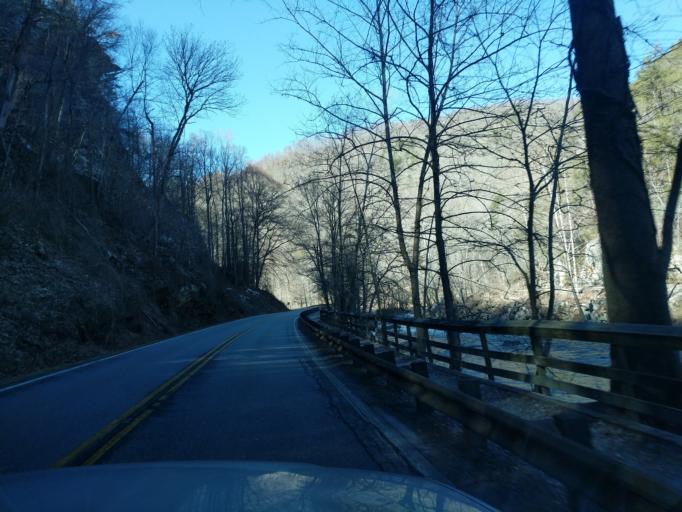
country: US
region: North Carolina
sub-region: Swain County
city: Bryson City
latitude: 35.3315
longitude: -83.5944
